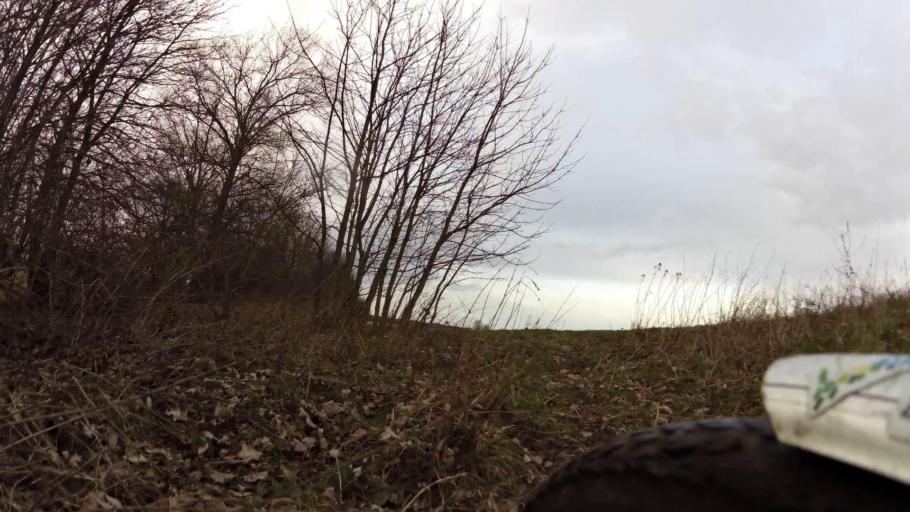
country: PL
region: West Pomeranian Voivodeship
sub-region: Powiat kamienski
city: Kamien Pomorski
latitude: 53.9361
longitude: 14.7621
